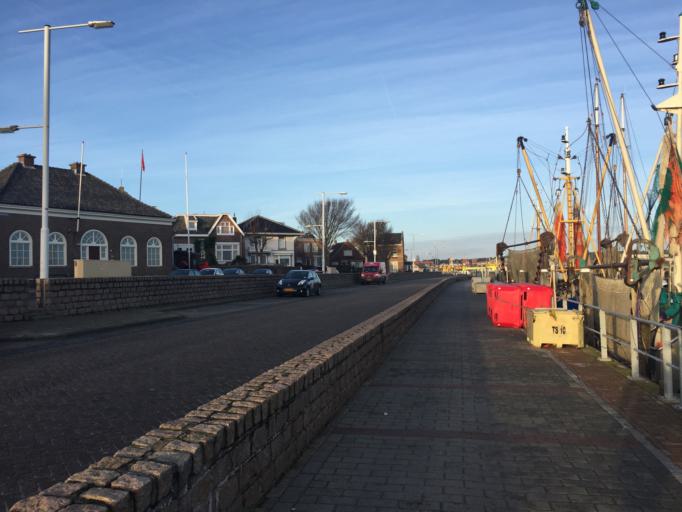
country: NL
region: Friesland
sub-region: Gemeente Terschelling
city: West-Terschelling
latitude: 53.3590
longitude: 5.2167
